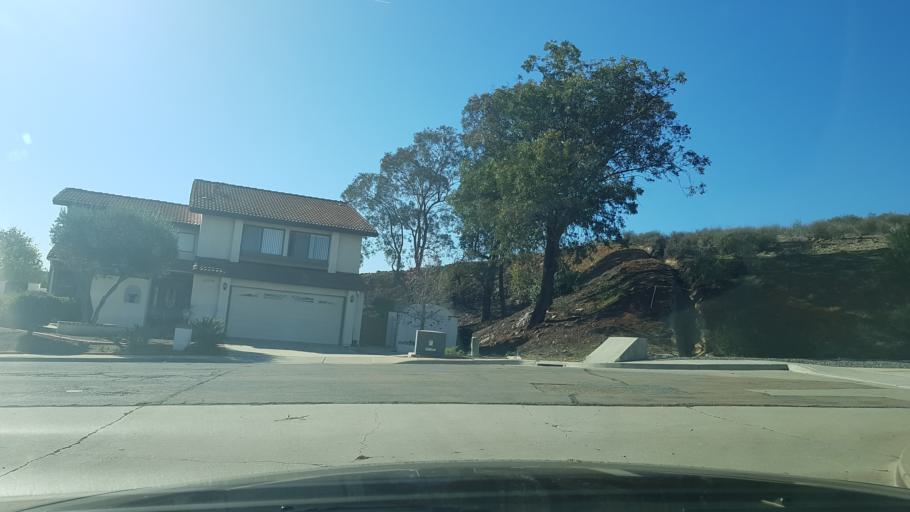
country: US
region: California
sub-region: San Diego County
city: Escondido
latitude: 33.0440
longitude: -117.0683
